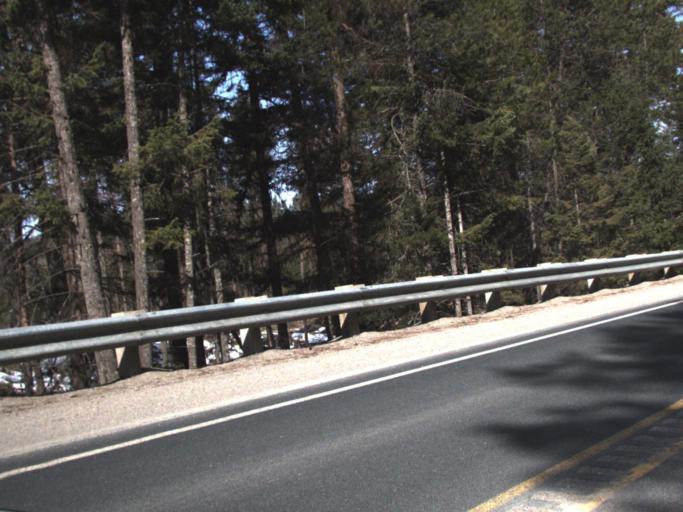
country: US
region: Washington
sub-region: Stevens County
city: Chewelah
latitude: 48.5051
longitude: -117.6728
